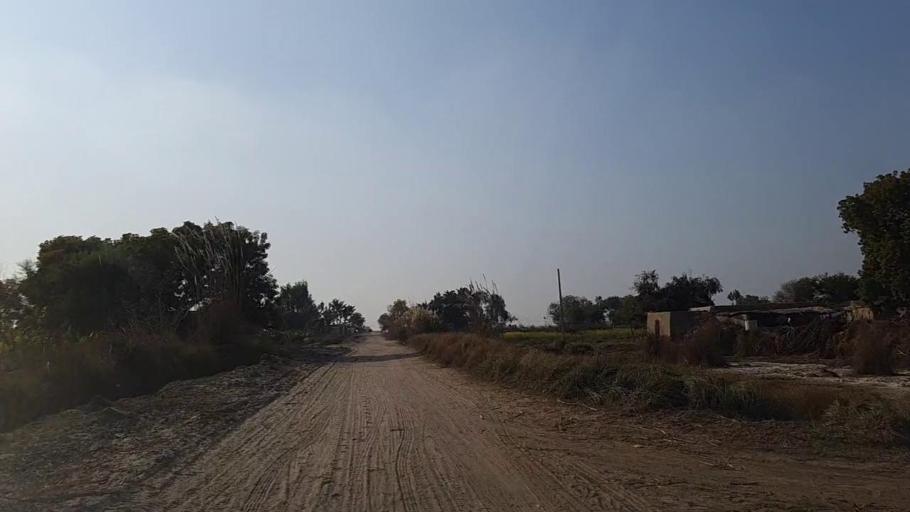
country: PK
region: Sindh
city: Daur
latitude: 26.4043
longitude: 68.2616
